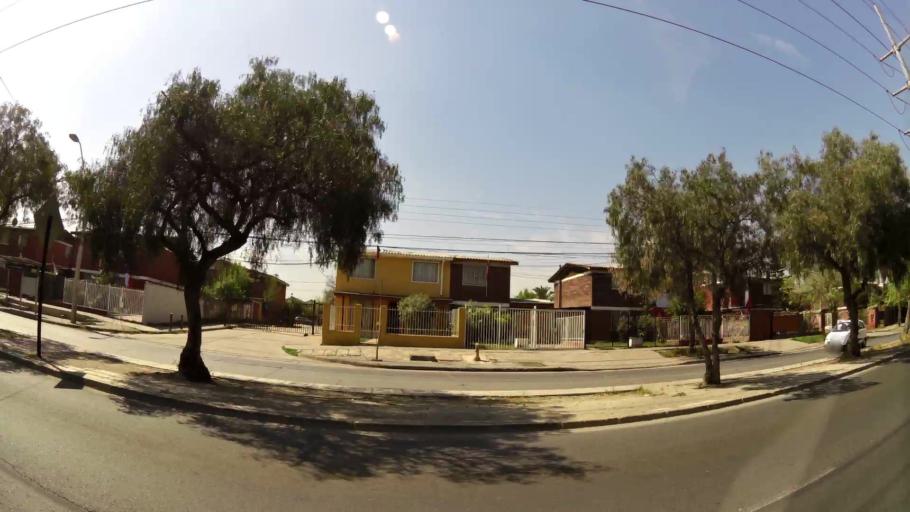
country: CL
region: Santiago Metropolitan
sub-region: Provincia de Santiago
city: La Pintana
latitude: -33.5576
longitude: -70.6011
